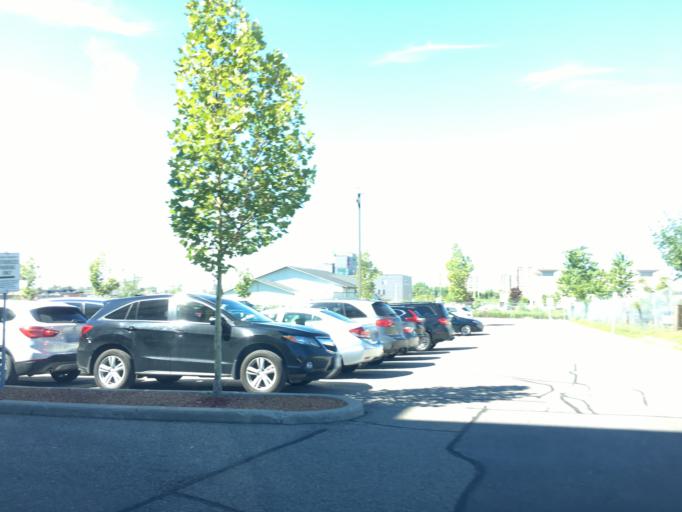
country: CA
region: Ontario
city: Scarborough
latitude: 43.8137
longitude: -79.2926
